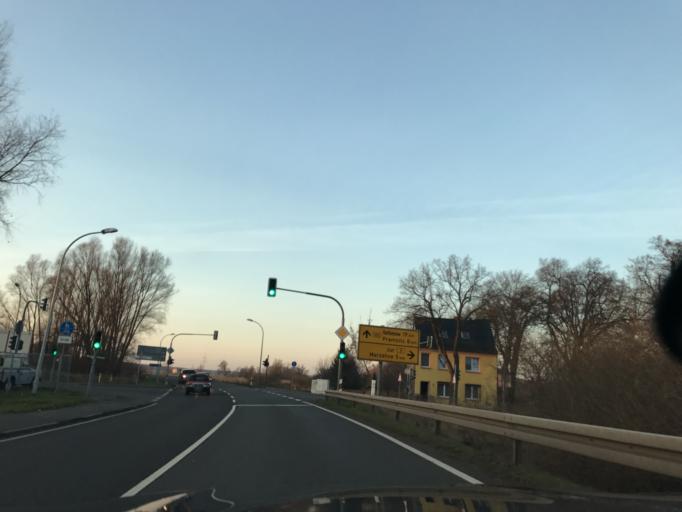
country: DE
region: Brandenburg
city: Nennhausen
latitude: 52.4981
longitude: 12.4591
